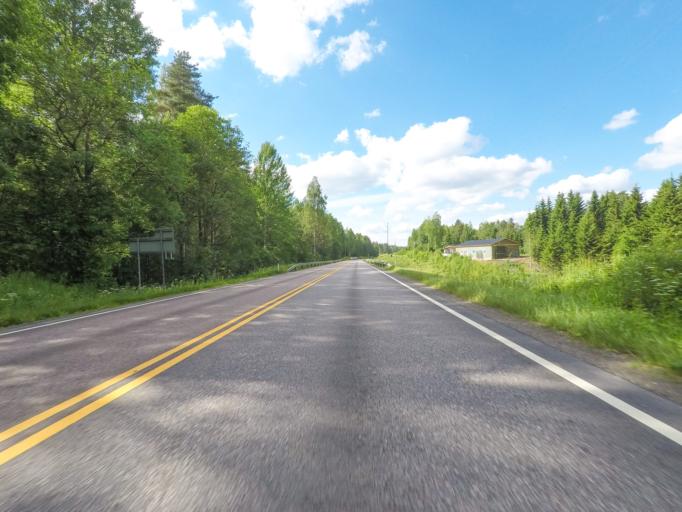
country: FI
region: Southern Savonia
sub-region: Savonlinna
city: Kerimaeki
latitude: 61.8694
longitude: 29.1285
